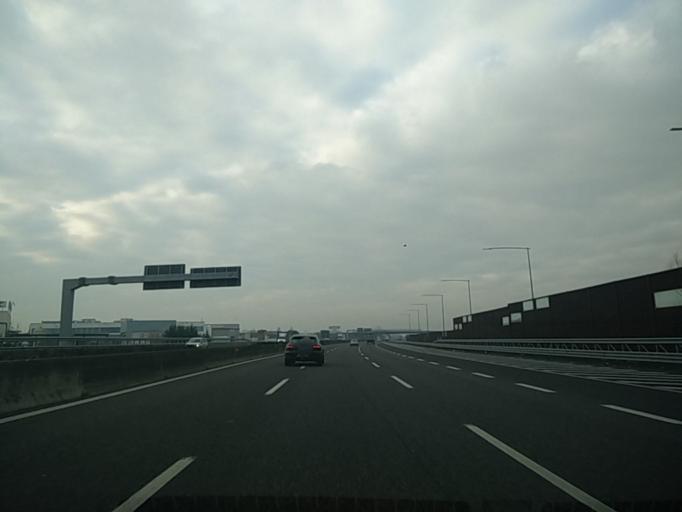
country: IT
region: Emilia-Romagna
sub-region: Forli-Cesena
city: Gatteo-Sant'Angelo
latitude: 44.1214
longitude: 12.3894
